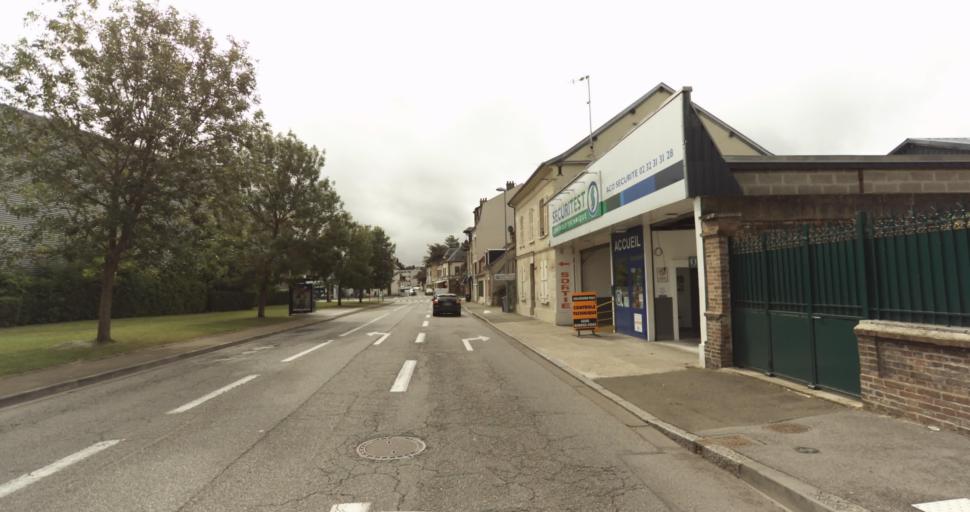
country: FR
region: Haute-Normandie
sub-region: Departement de l'Eure
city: Evreux
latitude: 49.0283
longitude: 1.1433
